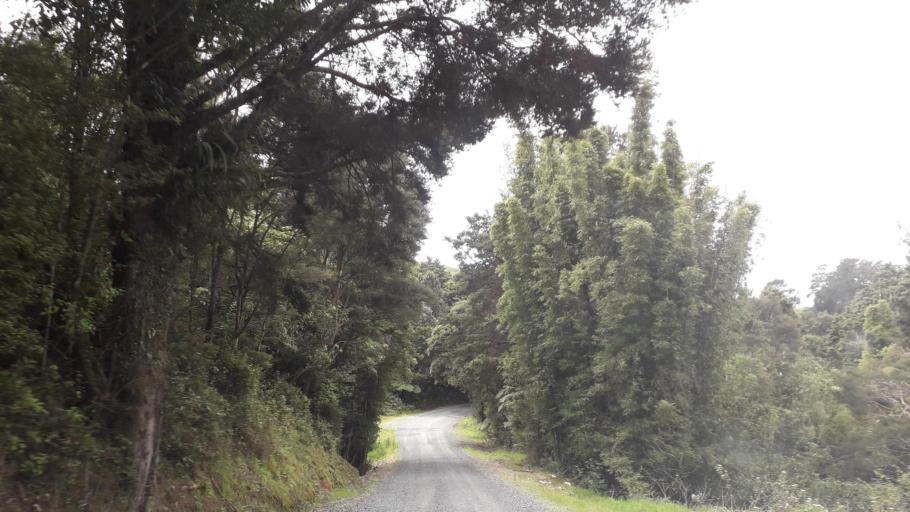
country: NZ
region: Northland
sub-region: Far North District
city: Taipa
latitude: -35.0825
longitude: 173.5500
